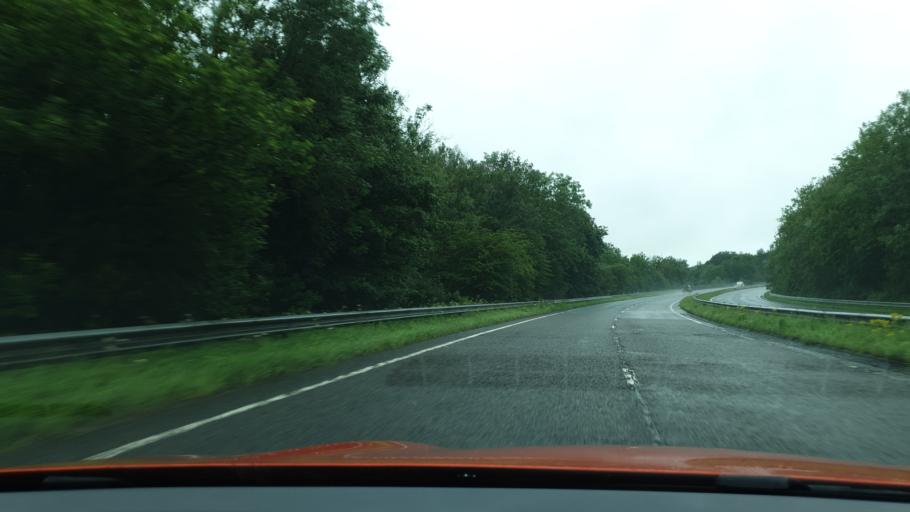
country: GB
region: England
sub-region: Cumbria
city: Grange-over-Sands
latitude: 54.2203
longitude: -2.8881
